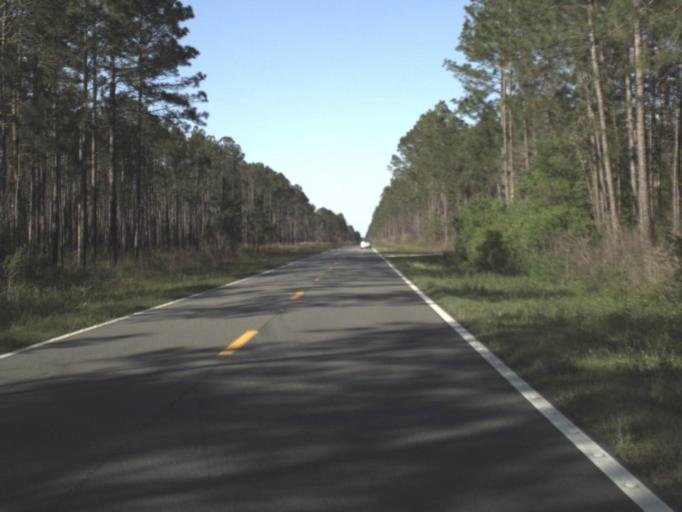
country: US
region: Florida
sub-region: Gulf County
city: Wewahitchka
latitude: 30.1387
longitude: -84.9818
